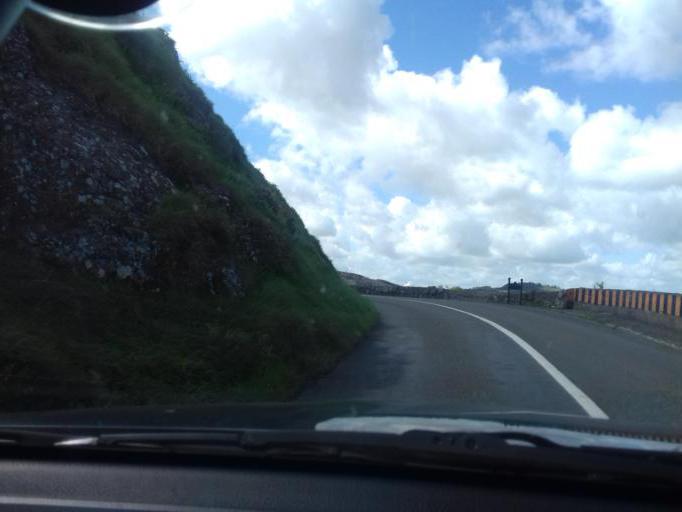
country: IE
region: Munster
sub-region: Waterford
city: Dunmore East
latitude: 52.2409
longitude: -6.9757
